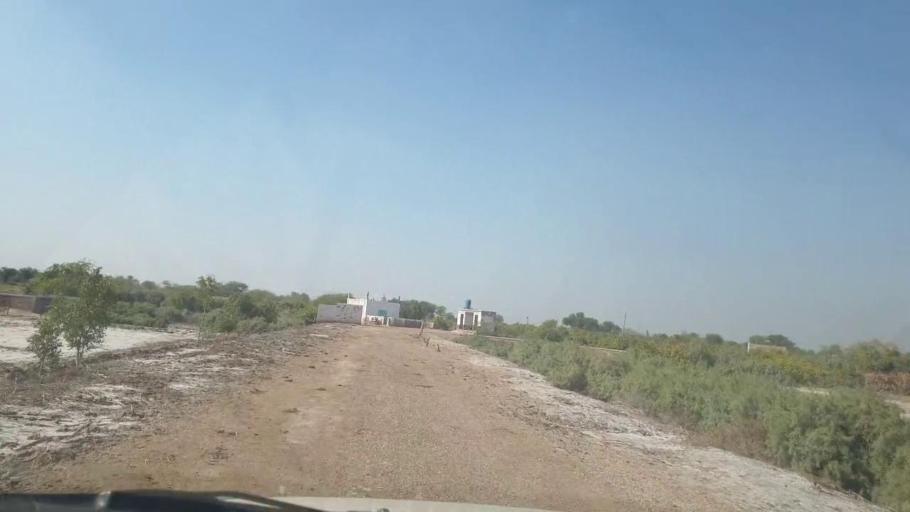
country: PK
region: Sindh
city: Mirpur Khas
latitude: 25.4783
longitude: 69.1178
